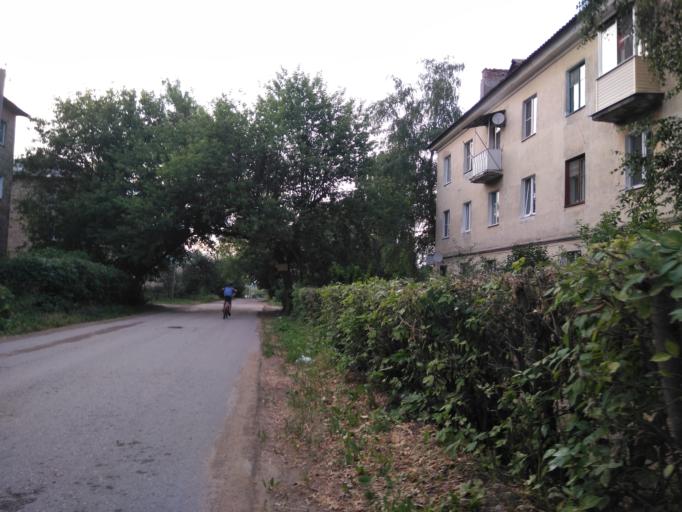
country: RU
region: Tula
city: Lomintsevskiy
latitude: 53.9359
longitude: 37.6243
